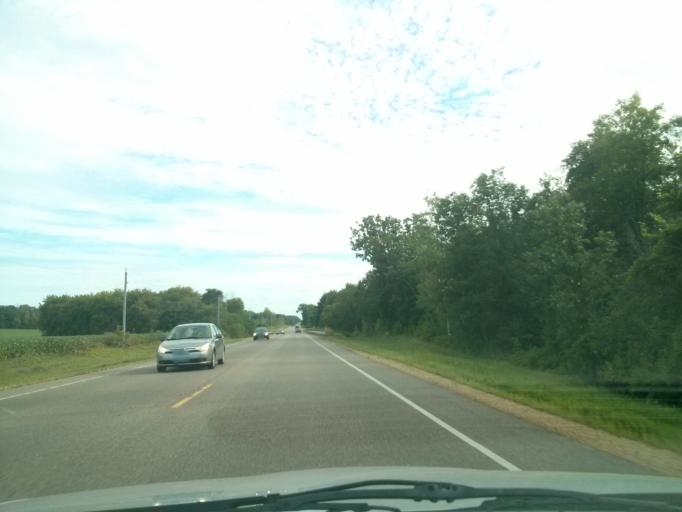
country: US
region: Minnesota
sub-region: Washington County
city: Lake Saint Croix Beach
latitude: 44.9300
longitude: -92.7316
